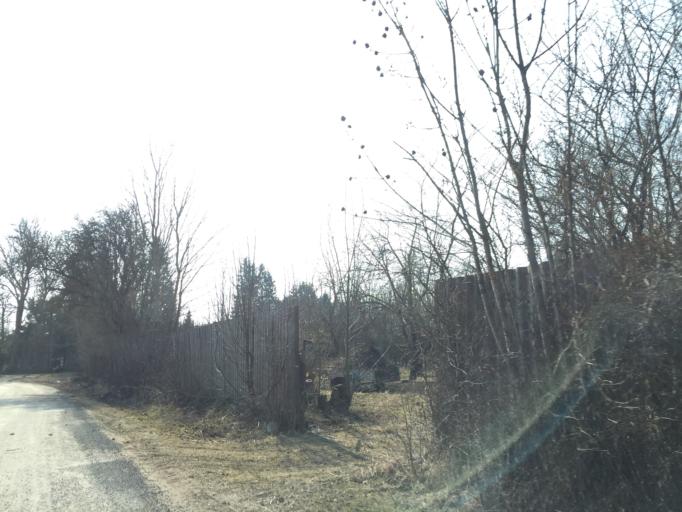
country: EE
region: Saare
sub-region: Kuressaare linn
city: Kuressaare
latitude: 58.3795
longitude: 22.7116
